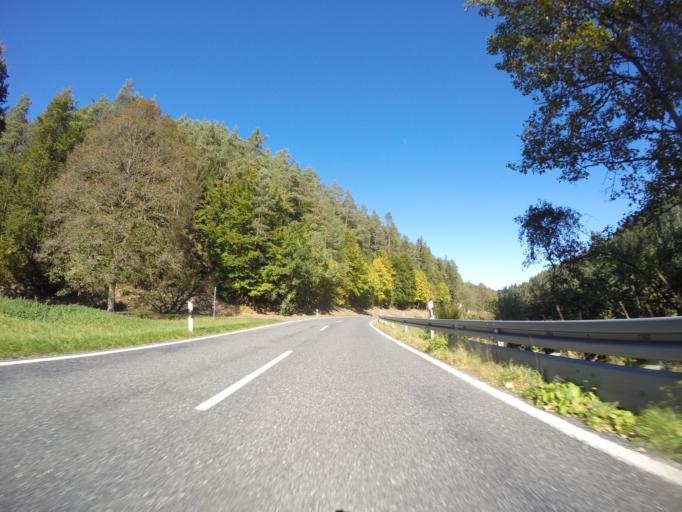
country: DE
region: Bavaria
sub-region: Upper Franconia
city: Gossweinstein
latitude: 49.8024
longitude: 11.3314
